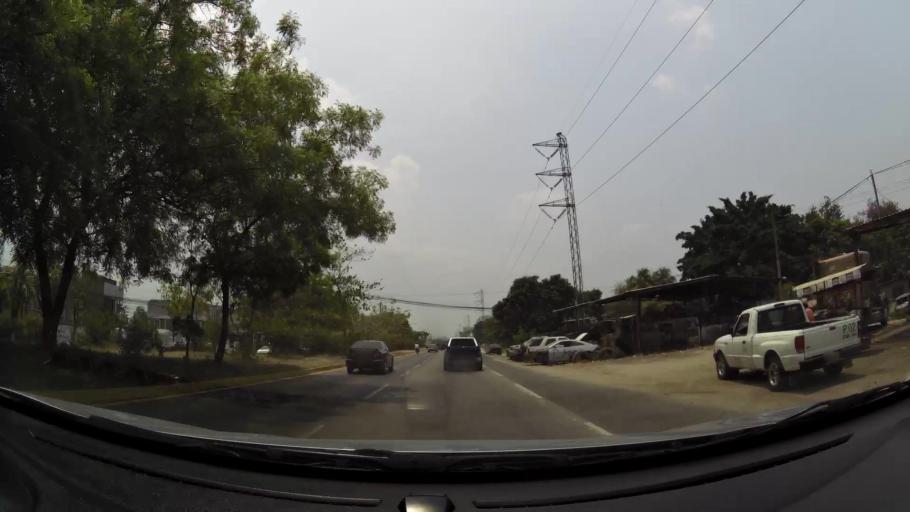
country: HN
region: Cortes
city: San Pedro Sula
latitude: 15.4820
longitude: -87.9776
